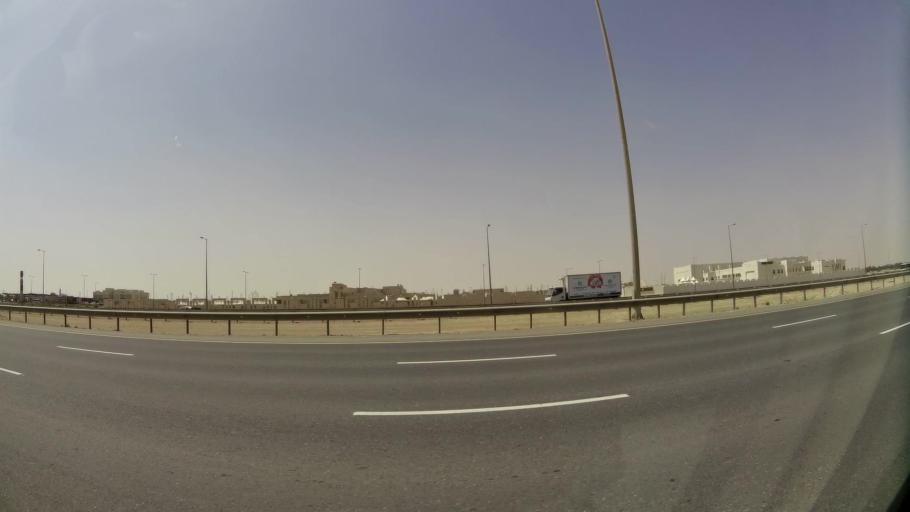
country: QA
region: Baladiyat Umm Salal
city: Umm Salal Muhammad
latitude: 25.4365
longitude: 51.4124
